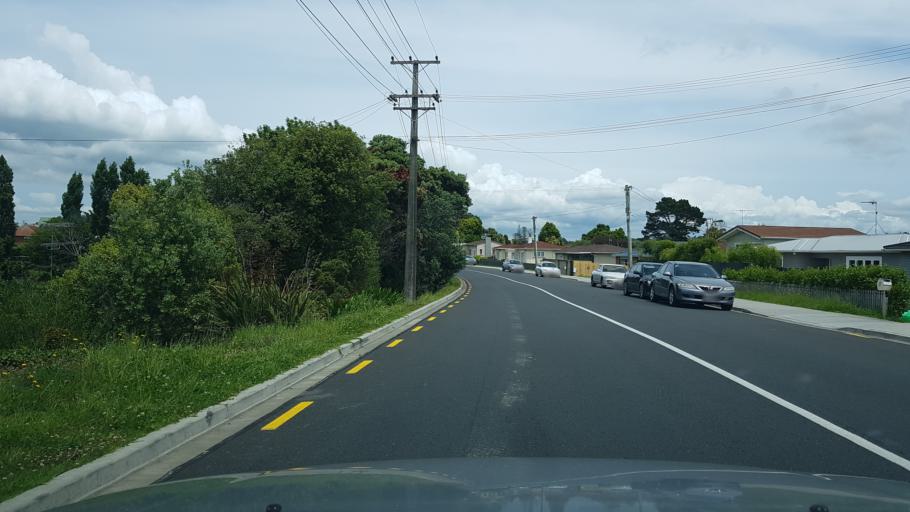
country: NZ
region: Auckland
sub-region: Auckland
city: North Shore
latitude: -36.7988
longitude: 174.7508
